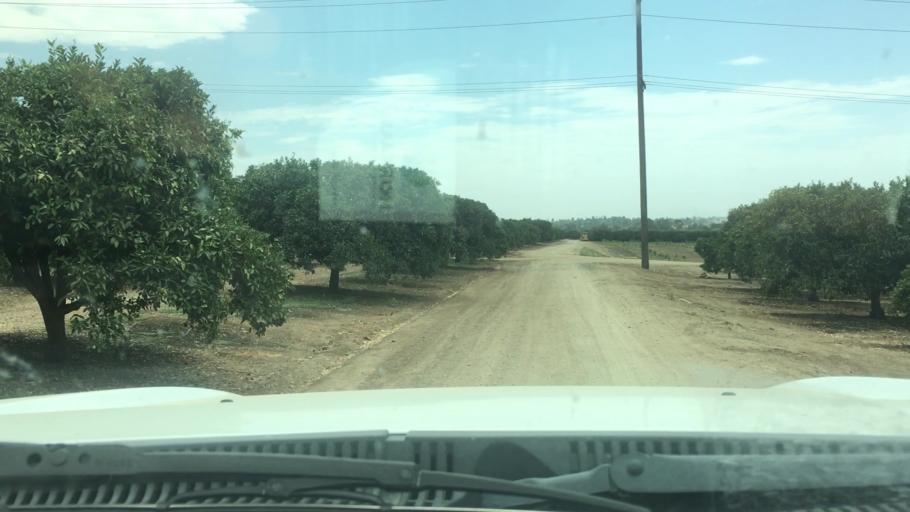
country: US
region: California
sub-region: Tulare County
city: Porterville
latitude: 36.0955
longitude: -119.0044
